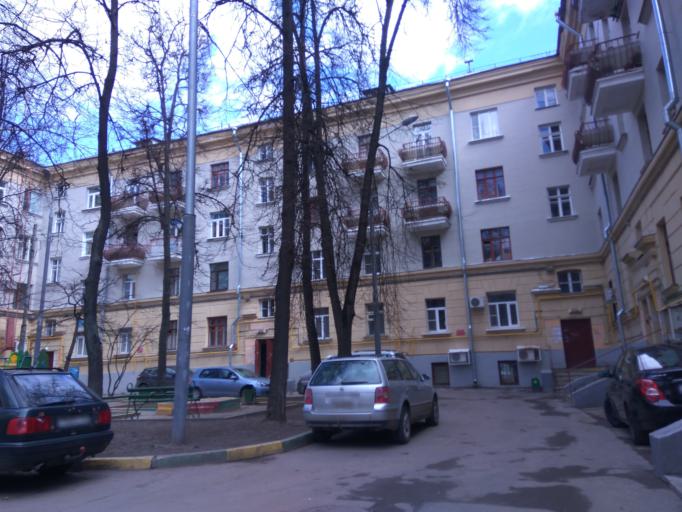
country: RU
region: Moskovskaya
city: Izmaylovo
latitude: 55.7927
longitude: 37.8014
